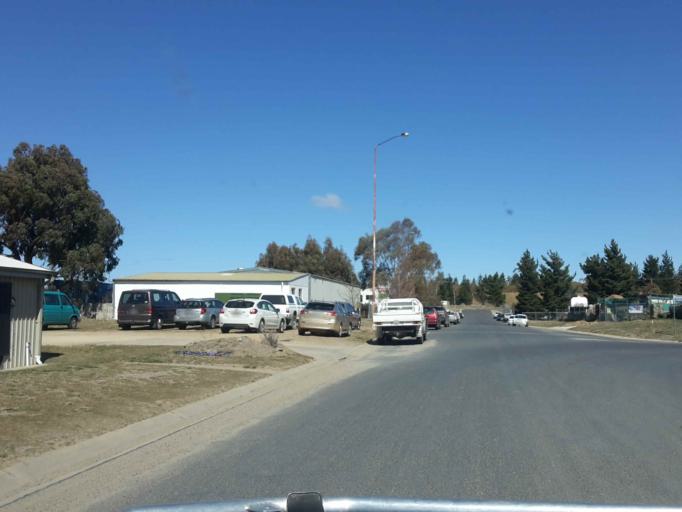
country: AU
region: New South Wales
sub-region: Snowy River
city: Jindabyne
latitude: -36.4374
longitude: 148.6037
